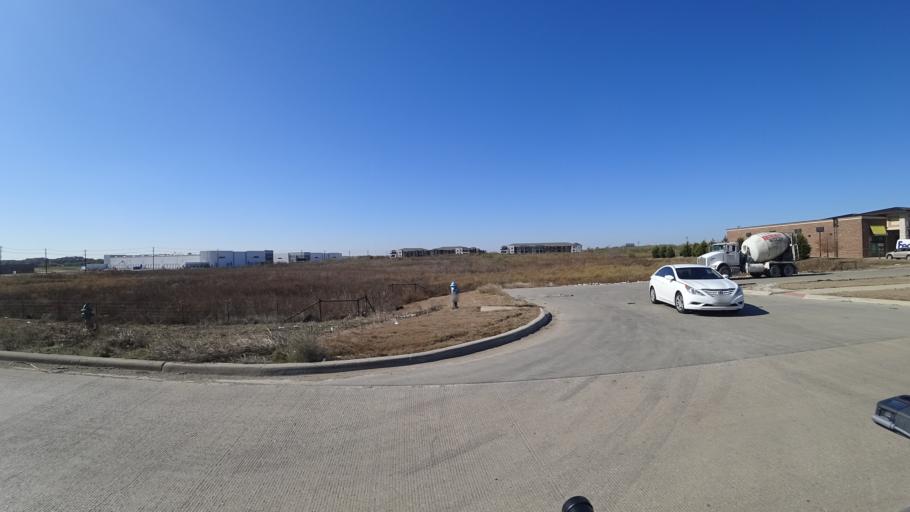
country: US
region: Texas
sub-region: Denton County
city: The Colony
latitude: 33.0486
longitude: -96.9271
